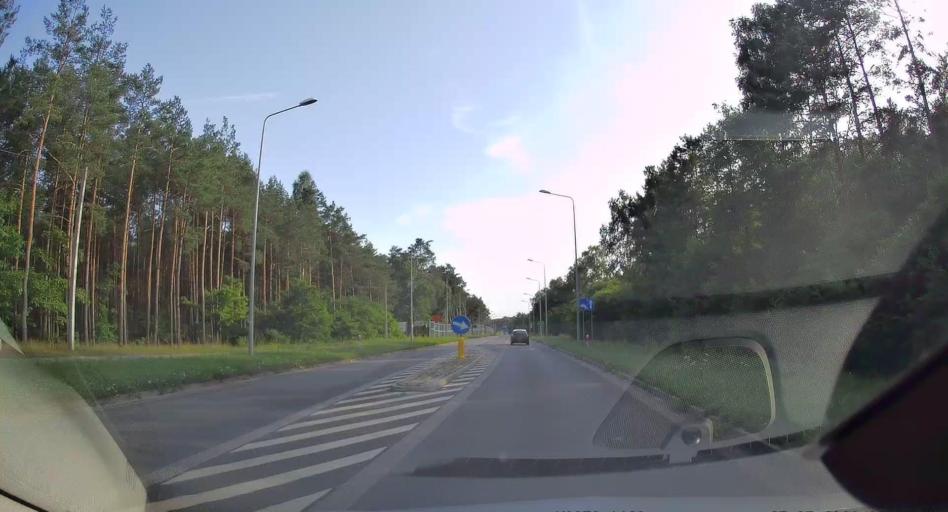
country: PL
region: Swietokrzyskie
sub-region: Powiat konecki
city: Konskie
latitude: 51.1232
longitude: 20.3556
